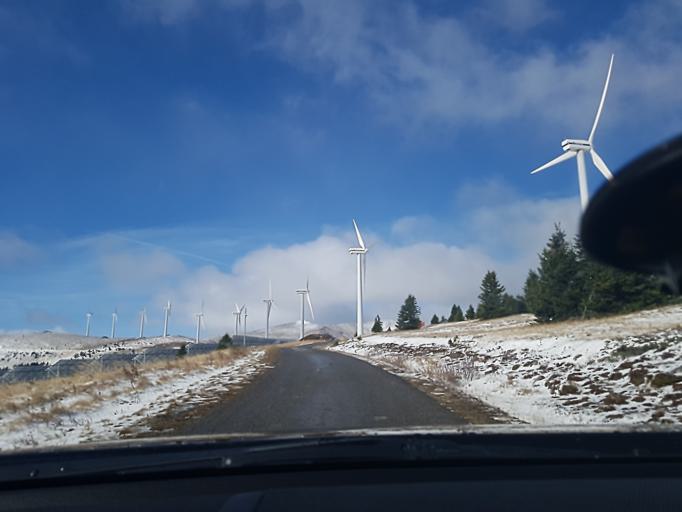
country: AT
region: Styria
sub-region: Politischer Bezirk Murtal
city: Pusterwald
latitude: 47.2732
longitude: 14.3961
